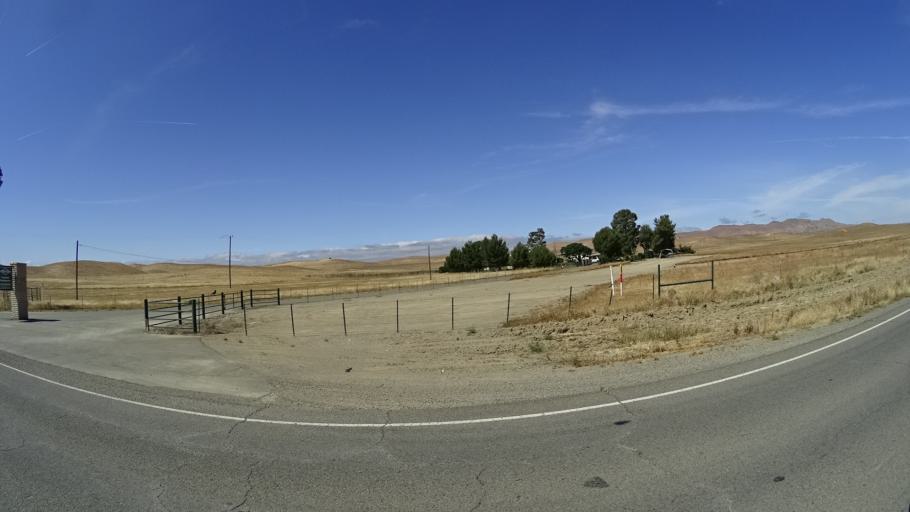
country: US
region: California
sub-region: Kings County
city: Avenal
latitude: 35.9064
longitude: -120.0604
